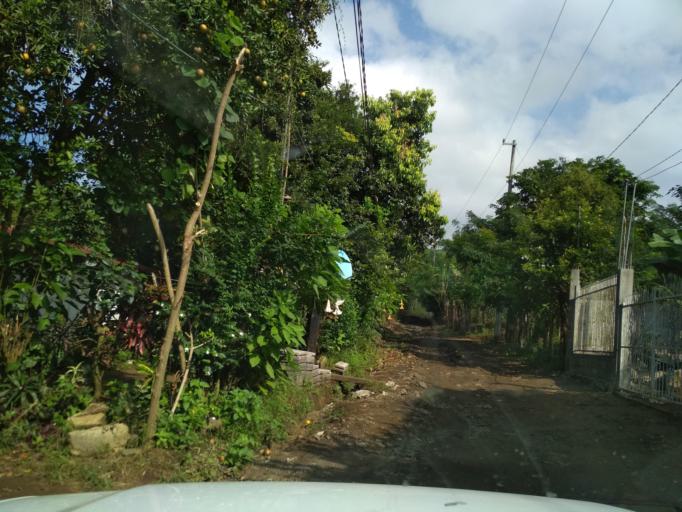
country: MX
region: Veracruz
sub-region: San Andres Tuxtla
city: Matacapan
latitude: 18.4420
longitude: -95.1736
